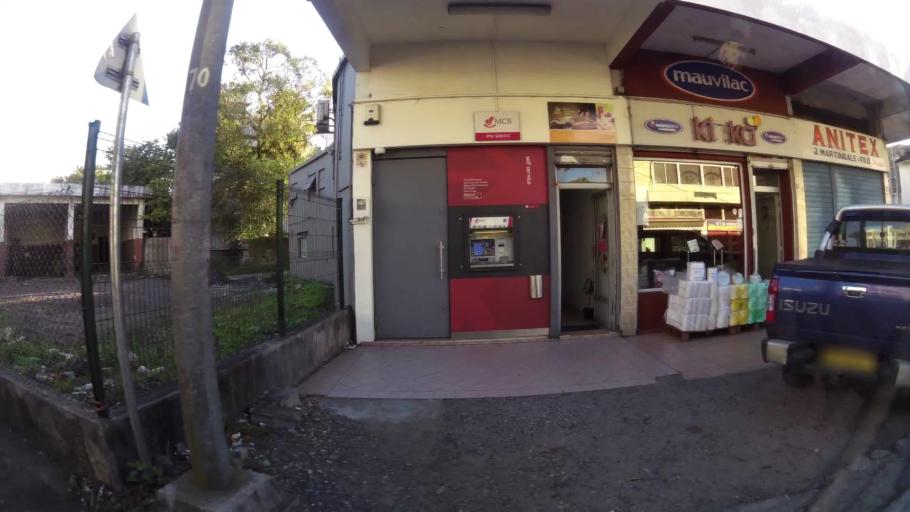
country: MU
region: Plaines Wilhems
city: Curepipe
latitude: -20.3131
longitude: 57.5237
